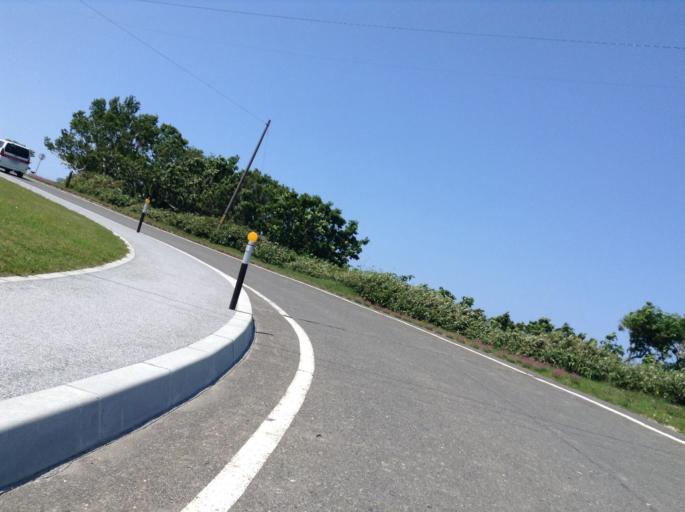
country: JP
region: Hokkaido
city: Wakkanai
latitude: 45.4202
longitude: 141.6691
